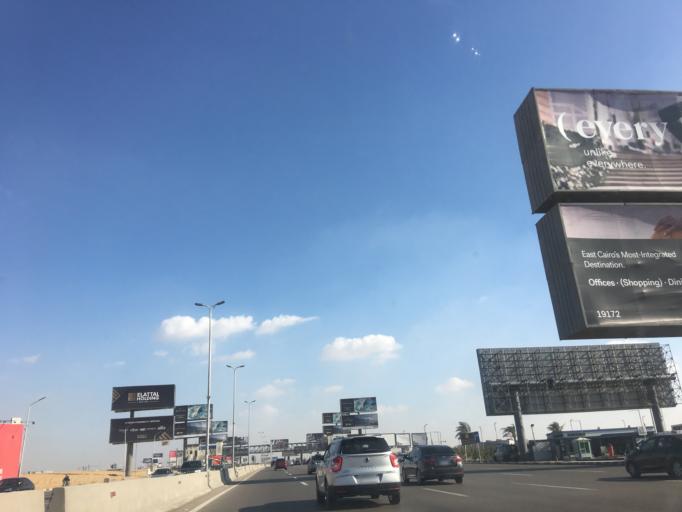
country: EG
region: Muhafazat al Qahirah
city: Cairo
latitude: 30.0176
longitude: 31.3895
